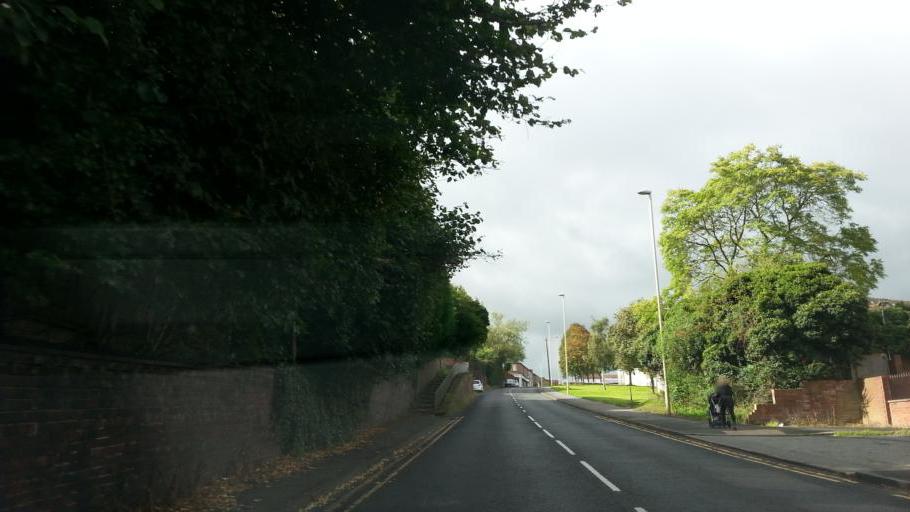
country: GB
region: England
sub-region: Dudley
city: Halesowen
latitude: 52.4463
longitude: -2.0544
